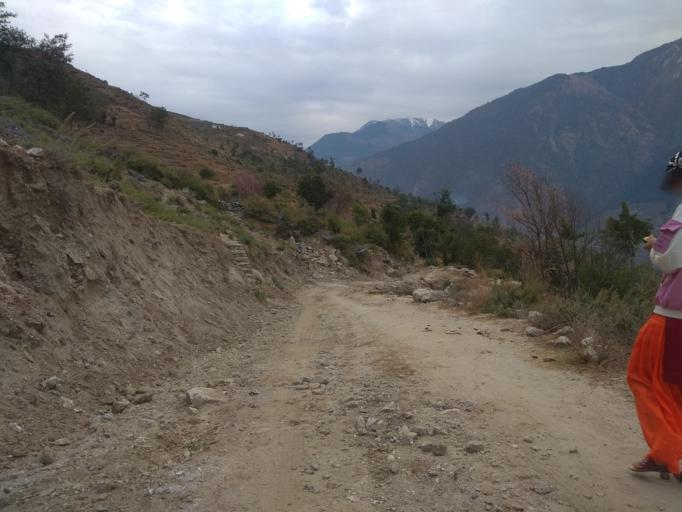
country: NP
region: Far Western
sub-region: Seti Zone
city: Achham
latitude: 29.2355
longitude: 81.6393
